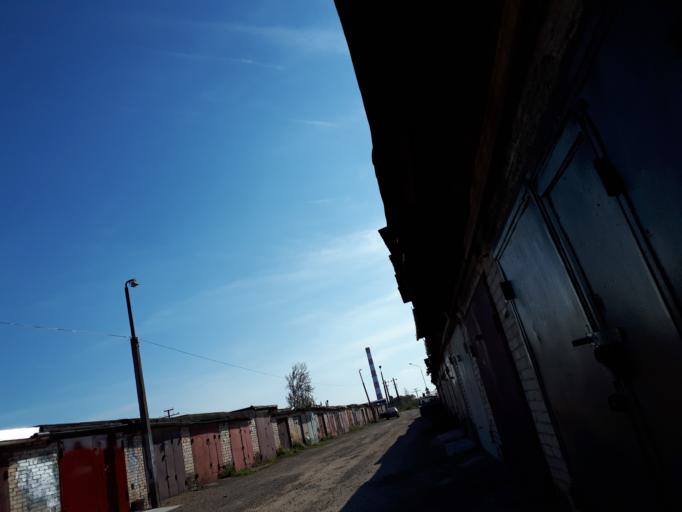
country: BY
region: Vitebsk
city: Vitebsk
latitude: 55.1648
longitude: 30.2446
